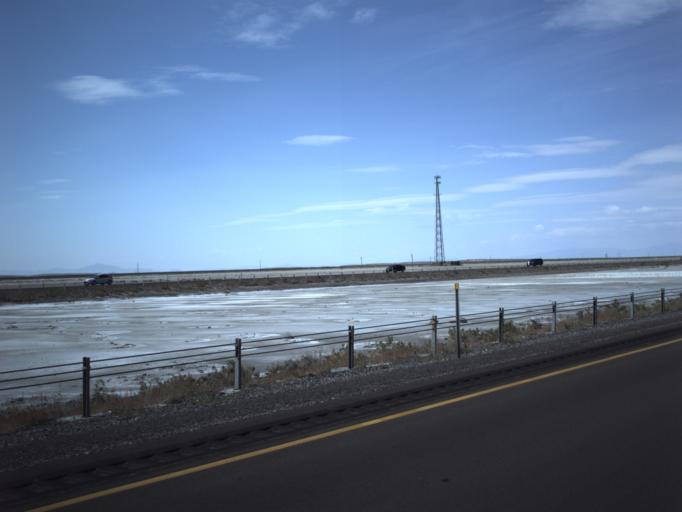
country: US
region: Utah
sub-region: Tooele County
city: Wendover
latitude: 40.7284
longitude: -113.3244
